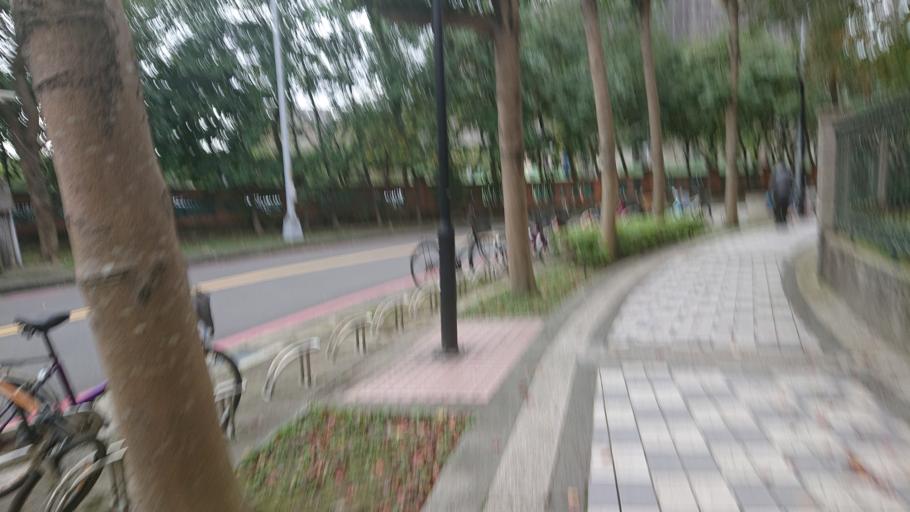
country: TW
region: Taiwan
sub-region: Taoyuan
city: Taoyuan
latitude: 24.9417
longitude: 121.3702
